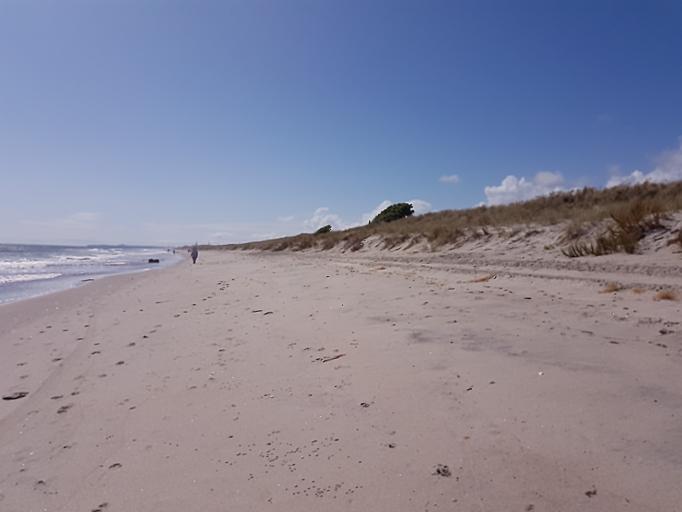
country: NZ
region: Bay of Plenty
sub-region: Western Bay of Plenty District
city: Maketu
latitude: -37.7060
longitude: 176.3153
